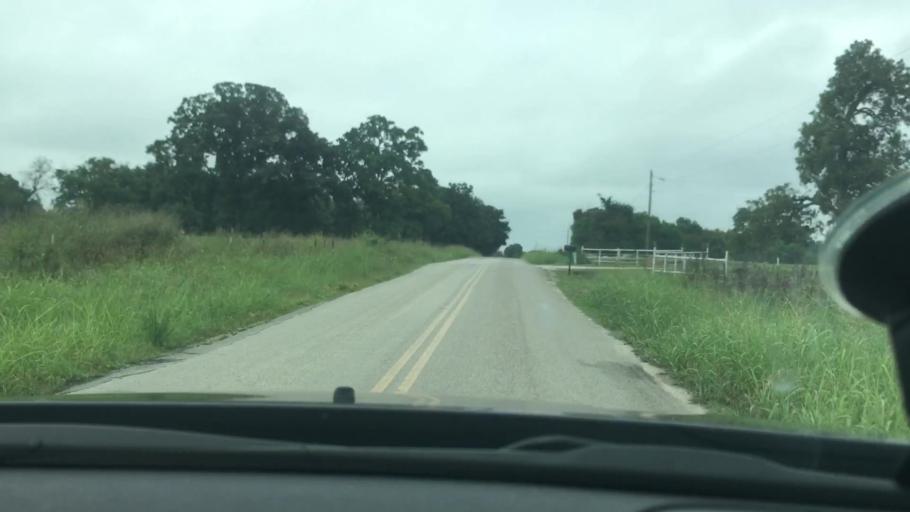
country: US
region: Oklahoma
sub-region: Pontotoc County
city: Ada
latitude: 34.8093
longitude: -96.7573
